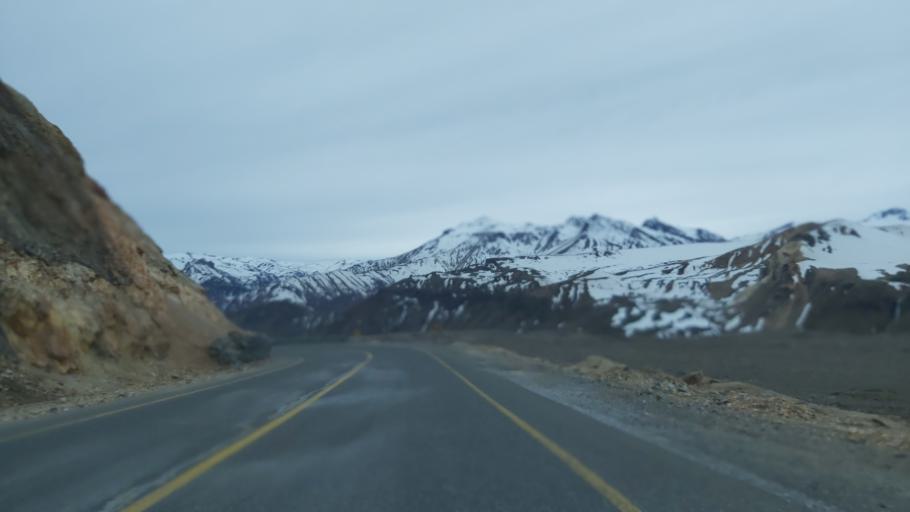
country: CL
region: Maule
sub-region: Provincia de Linares
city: Colbun
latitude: -35.9736
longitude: -70.5641
